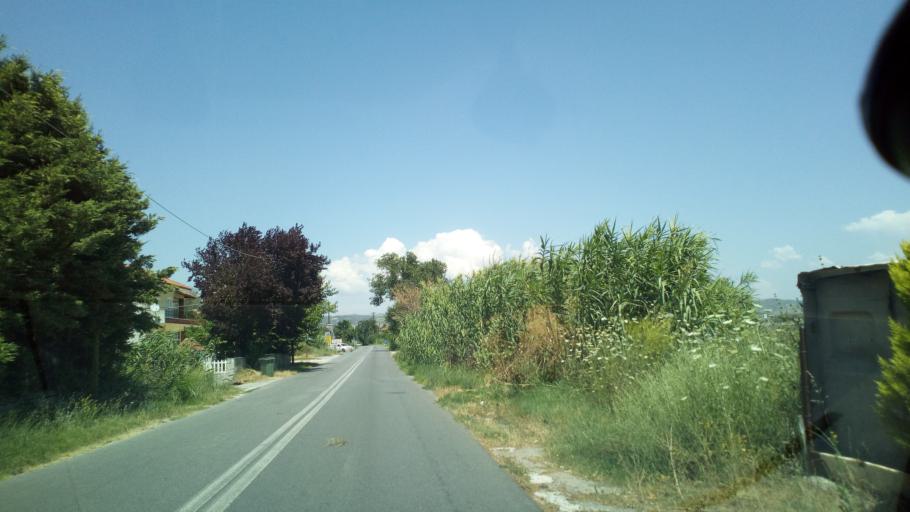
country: GR
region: Central Macedonia
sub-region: Nomos Thessalonikis
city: Lagkadas
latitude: 40.7483
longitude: 23.0731
